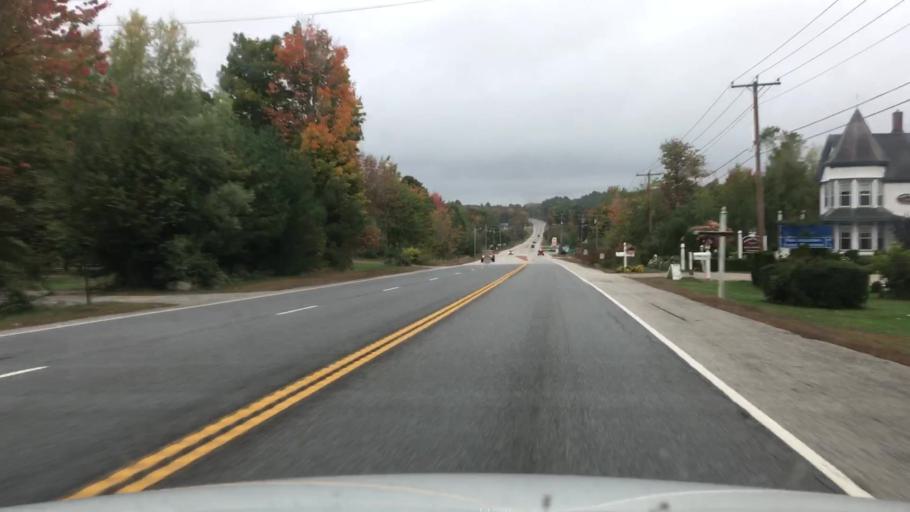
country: US
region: Maine
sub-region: Androscoggin County
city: Poland
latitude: 44.0104
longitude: -70.3623
